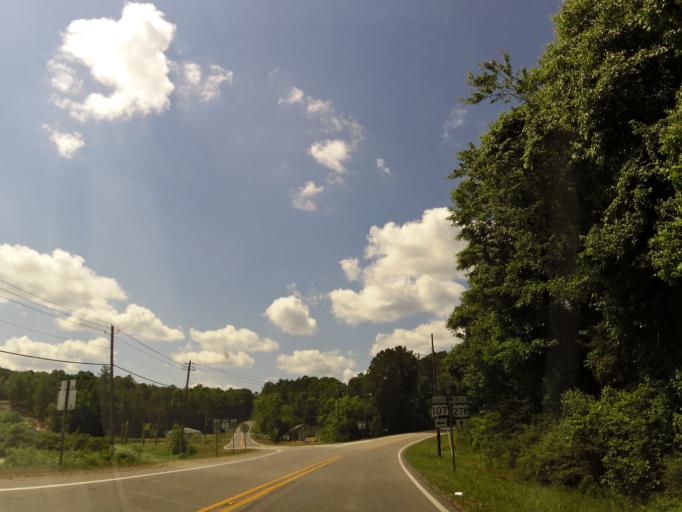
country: US
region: Alabama
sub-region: Marion County
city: Guin
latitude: 33.9621
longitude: -87.9146
